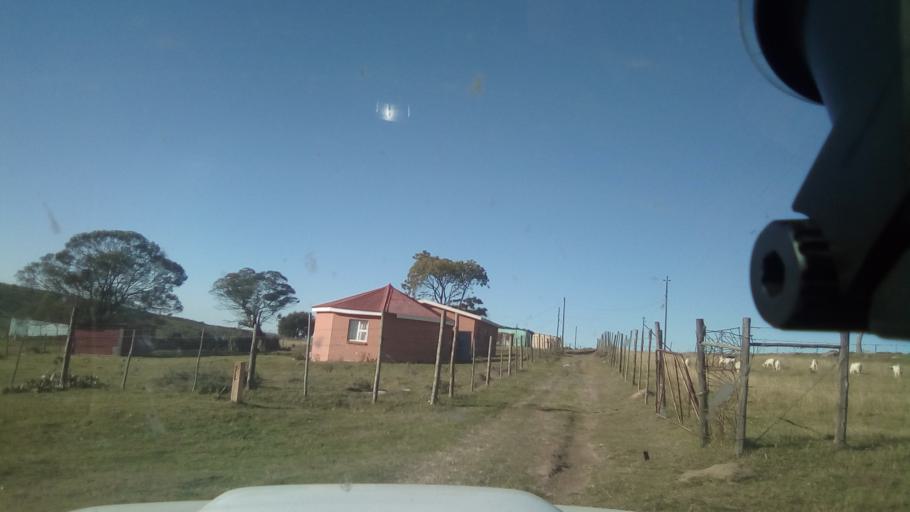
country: ZA
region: Eastern Cape
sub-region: Buffalo City Metropolitan Municipality
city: Bhisho
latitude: -32.9464
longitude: 27.2917
